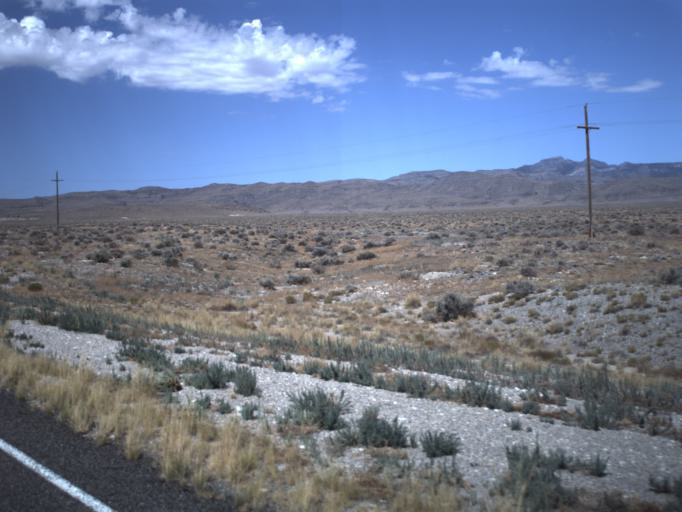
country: US
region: Utah
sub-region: Millard County
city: Delta
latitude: 39.0764
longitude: -113.2072
